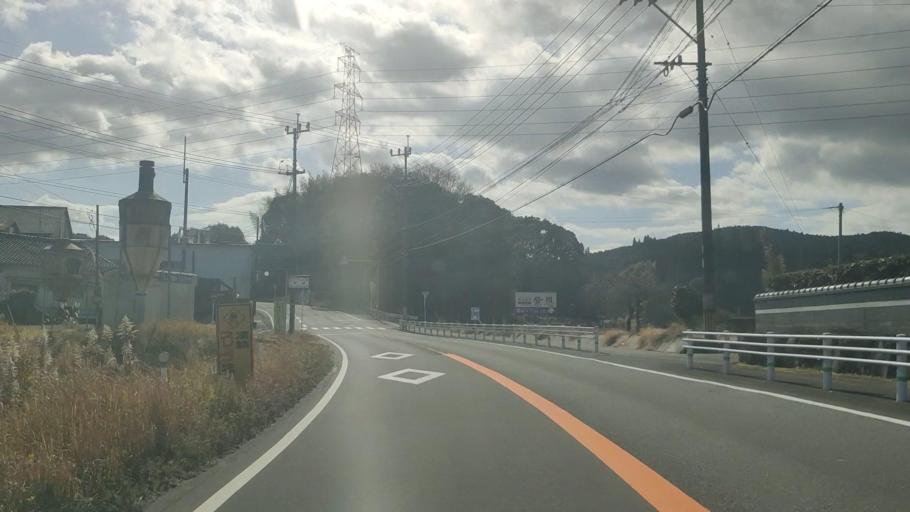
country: JP
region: Kagoshima
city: Okuchi-shinohara
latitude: 31.9341
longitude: 130.7030
